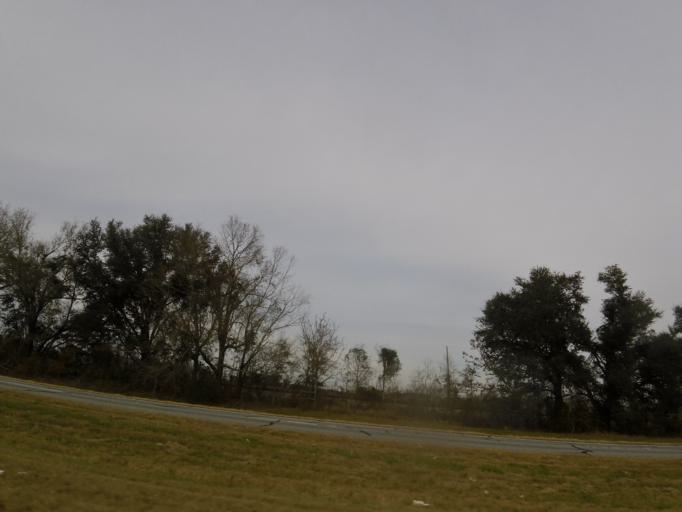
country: US
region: Georgia
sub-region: Seminole County
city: Donalsonville
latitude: 30.9999
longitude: -84.7820
